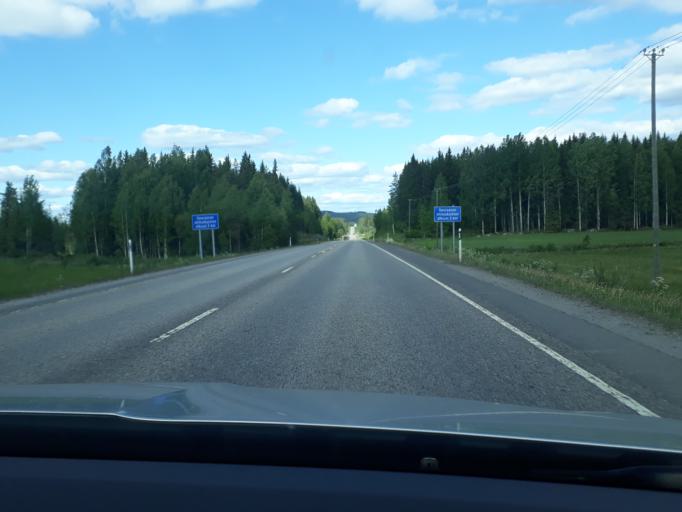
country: FI
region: Central Finland
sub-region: AEaenekoski
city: AEaenekoski
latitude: 62.6490
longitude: 25.7142
